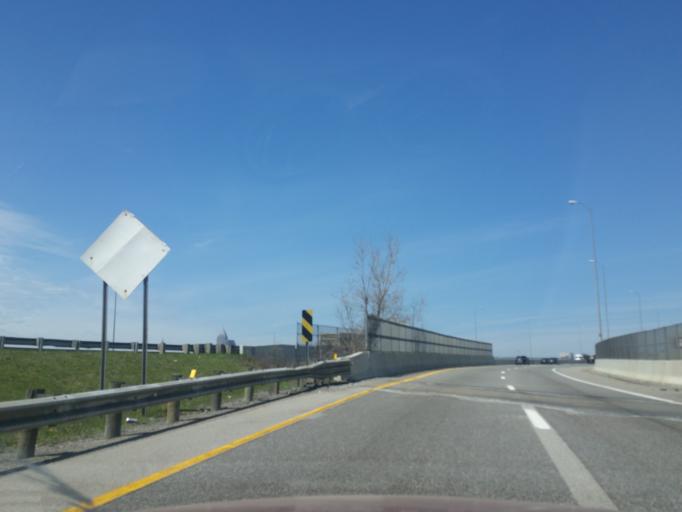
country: US
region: Ohio
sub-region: Cuyahoga County
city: Newburgh Heights
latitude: 41.4823
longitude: -81.6620
